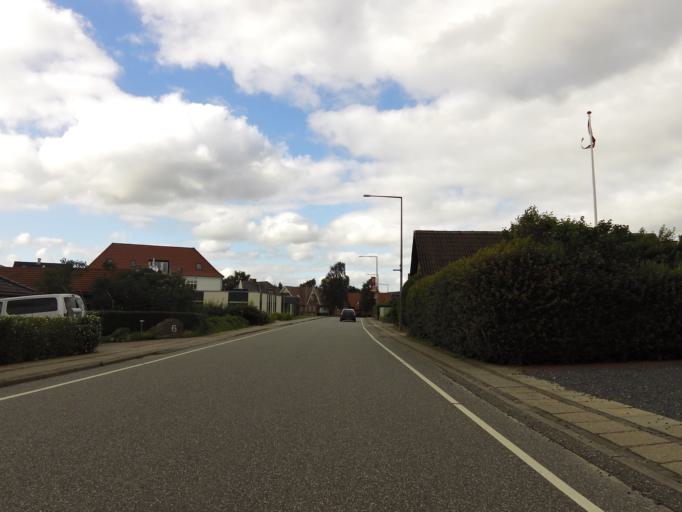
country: DK
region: South Denmark
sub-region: Kolding Kommune
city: Vamdrup
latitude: 55.3554
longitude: 9.1985
